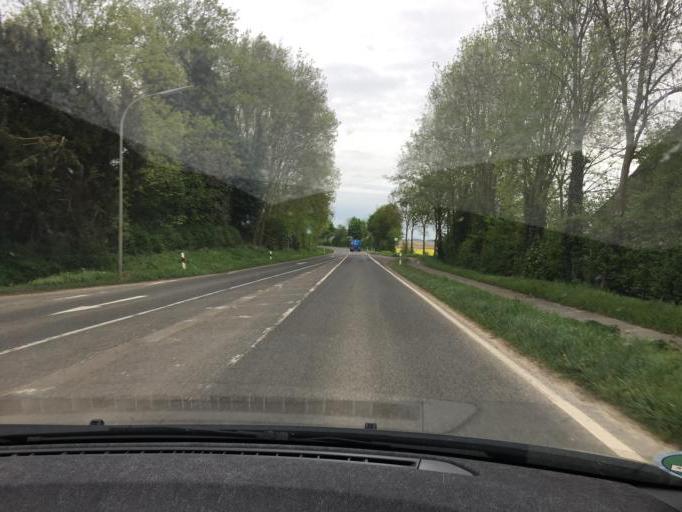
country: DE
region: North Rhine-Westphalia
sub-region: Regierungsbezirk Koln
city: Titz
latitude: 51.0586
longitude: 6.4287
